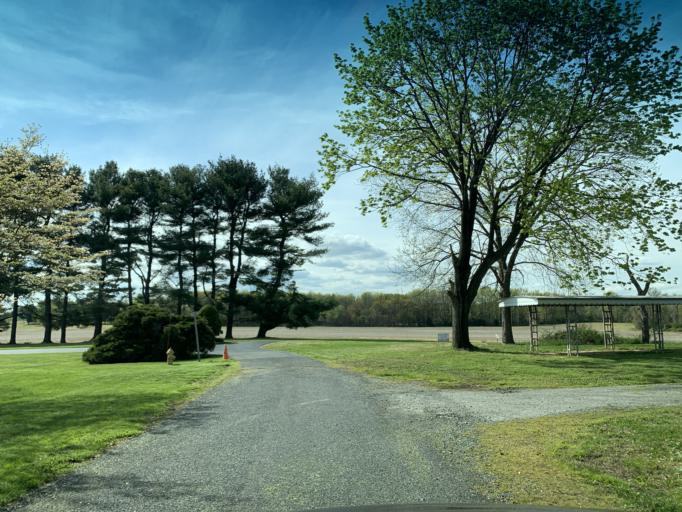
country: US
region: Maryland
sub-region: Harford County
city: Perryman
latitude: 39.4696
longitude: -76.2072
